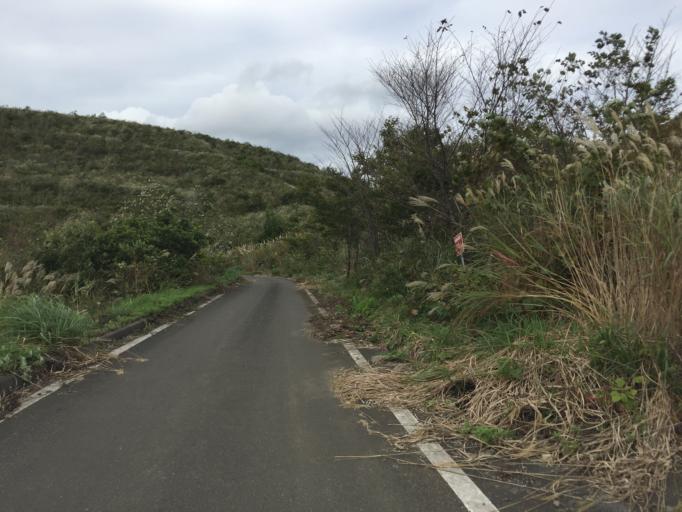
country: JP
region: Miyagi
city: Marumori
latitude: 37.9080
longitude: 140.7031
